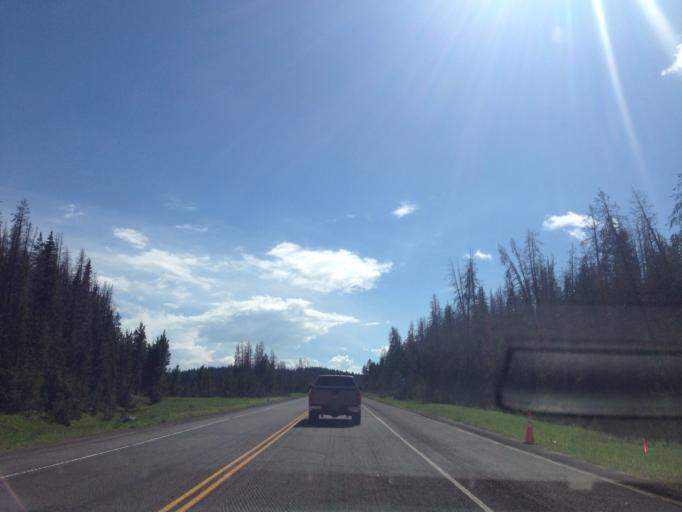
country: US
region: Colorado
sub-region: Routt County
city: Steamboat Springs
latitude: 40.3792
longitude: -106.7171
